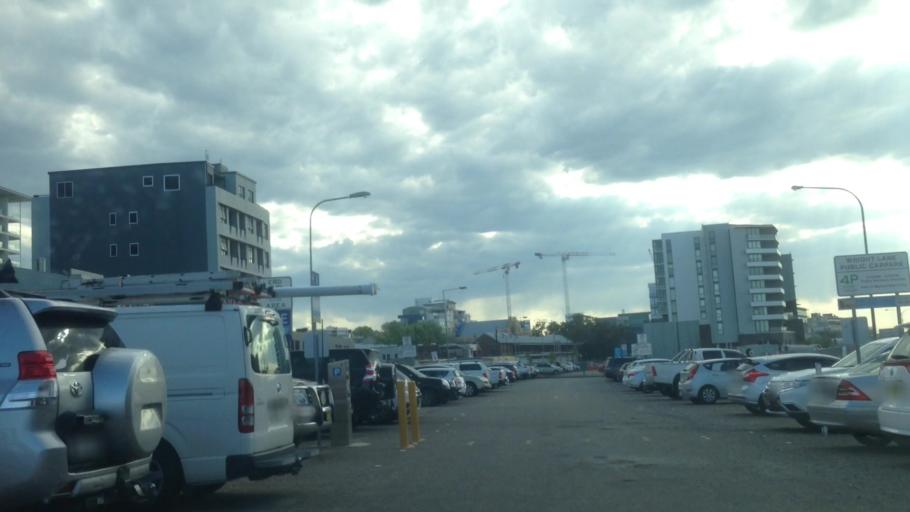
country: AU
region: New South Wales
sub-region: Newcastle
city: Cooks Hill
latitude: -32.9265
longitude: 151.7703
